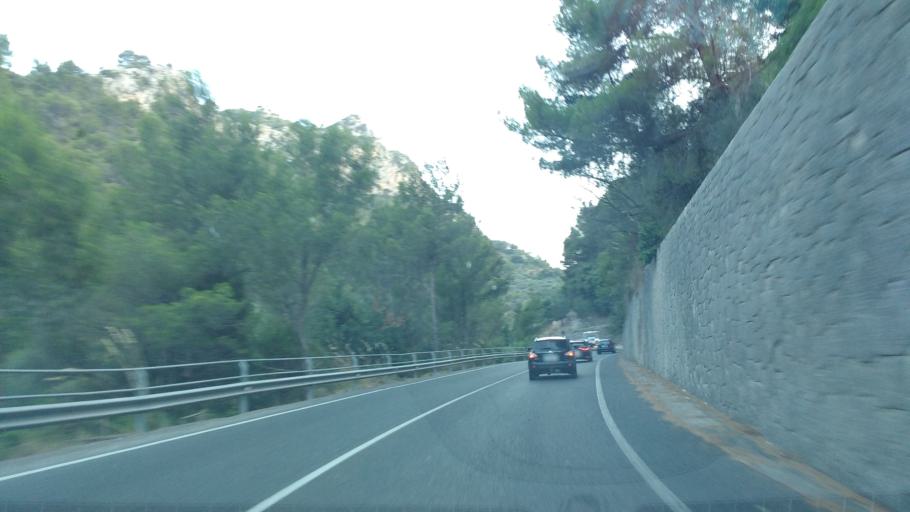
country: ES
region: Balearic Islands
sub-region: Illes Balears
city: Soller
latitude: 39.7530
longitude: 2.7066
